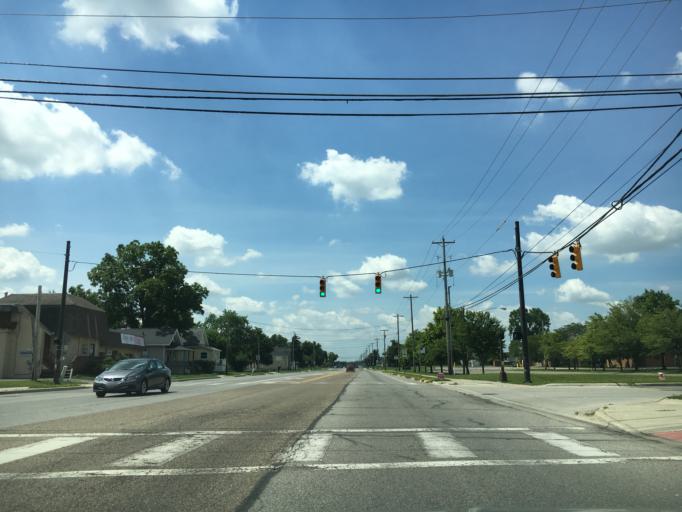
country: US
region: Ohio
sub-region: Franklin County
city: Lincoln Village
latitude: 39.9496
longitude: -83.1402
